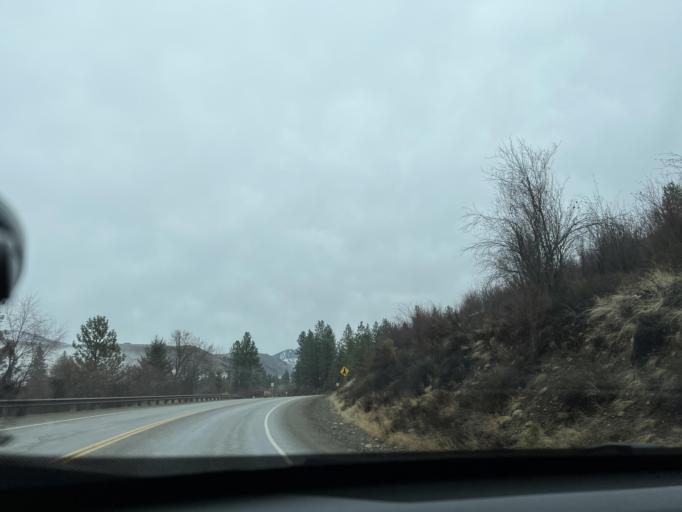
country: US
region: Washington
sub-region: Okanogan County
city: Brewster
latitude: 48.4724
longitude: -120.1895
